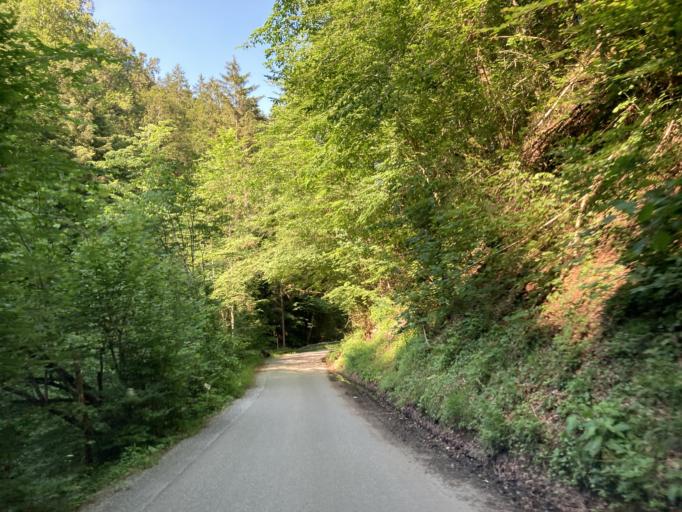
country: DE
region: Bavaria
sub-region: Upper Bavaria
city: Nussdorf am Inn
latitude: 47.7446
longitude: 12.1779
